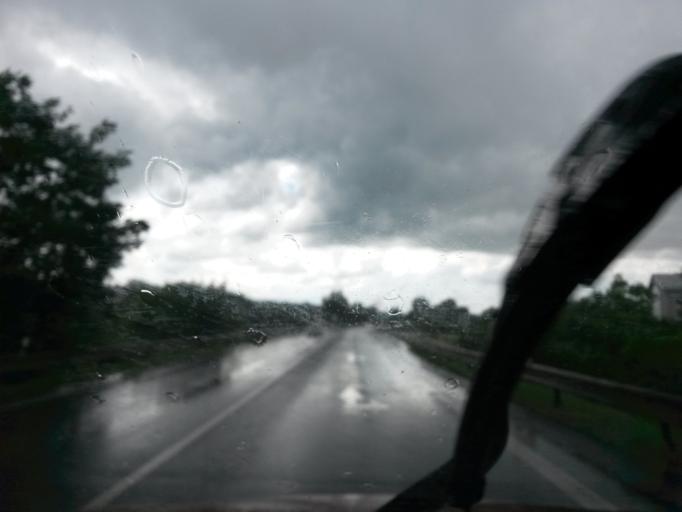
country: SK
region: Presovsky
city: Vranov nad Topl'ou
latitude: 48.8832
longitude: 21.6839
